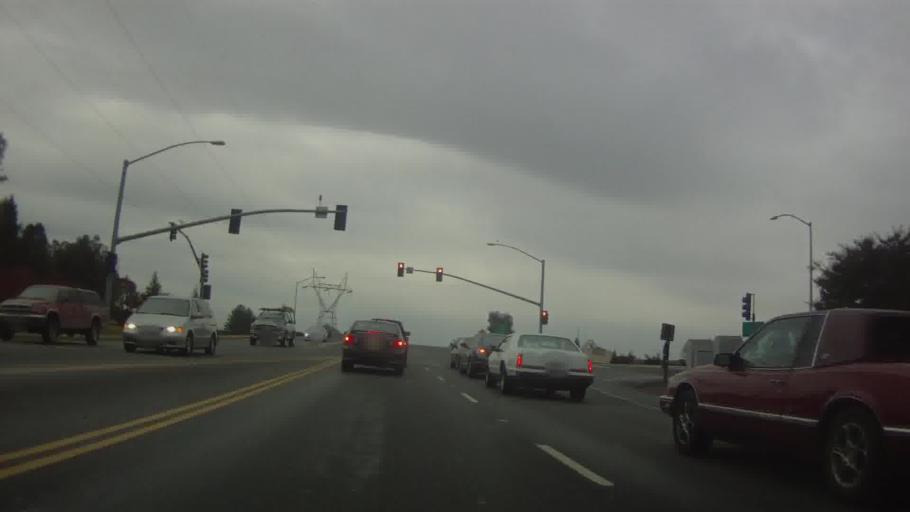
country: US
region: California
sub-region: Shasta County
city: Redding
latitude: 40.5836
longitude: -122.3578
